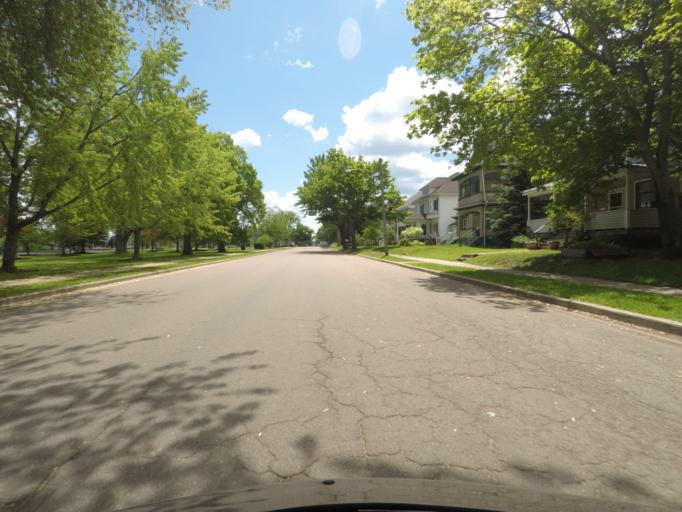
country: CA
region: New Brunswick
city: Moncton
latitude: 46.0928
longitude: -64.7906
